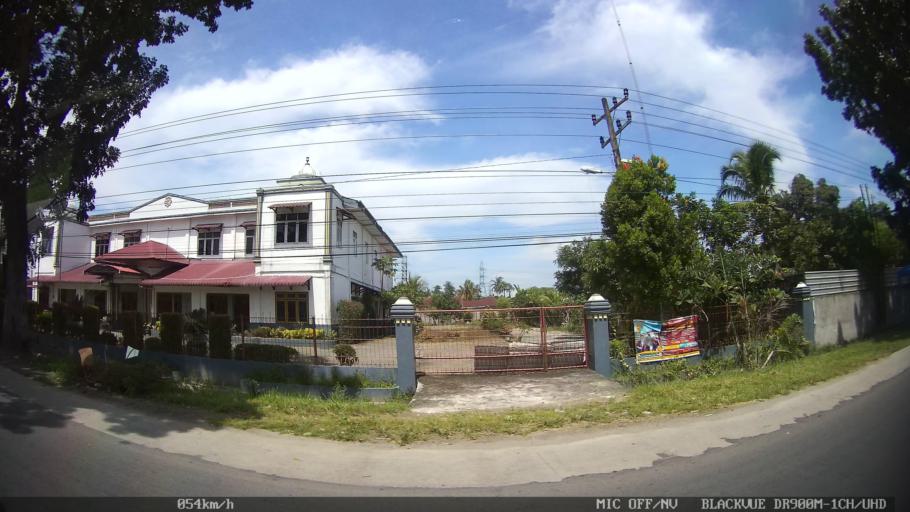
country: ID
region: North Sumatra
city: Binjai
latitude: 3.6474
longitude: 98.5101
